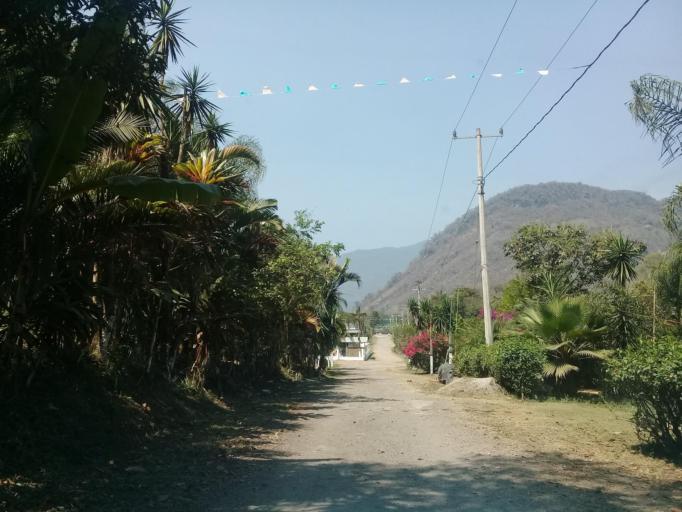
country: MX
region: Veracruz
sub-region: Ixtaczoquitlan
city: Capoluca
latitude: 18.8038
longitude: -96.9875
